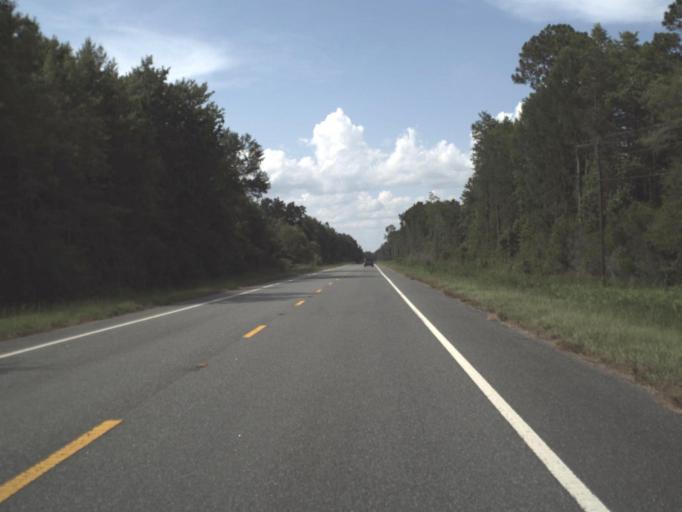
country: US
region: Florida
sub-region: Taylor County
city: Perry
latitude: 30.2608
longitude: -83.6252
